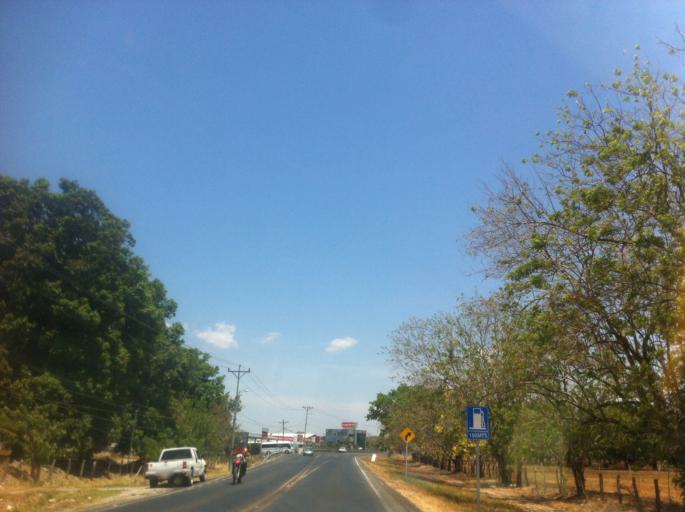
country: CR
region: Guanacaste
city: Sardinal
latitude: 10.5533
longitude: -85.5917
